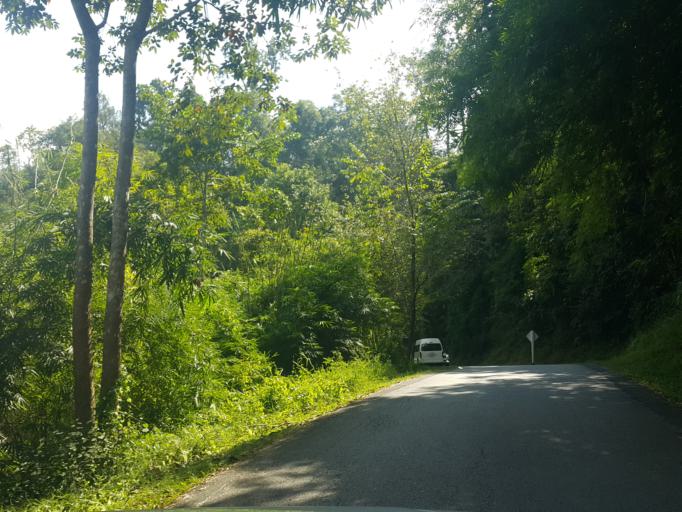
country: TH
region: Chiang Mai
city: Chom Thong
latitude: 18.5405
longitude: 98.6002
